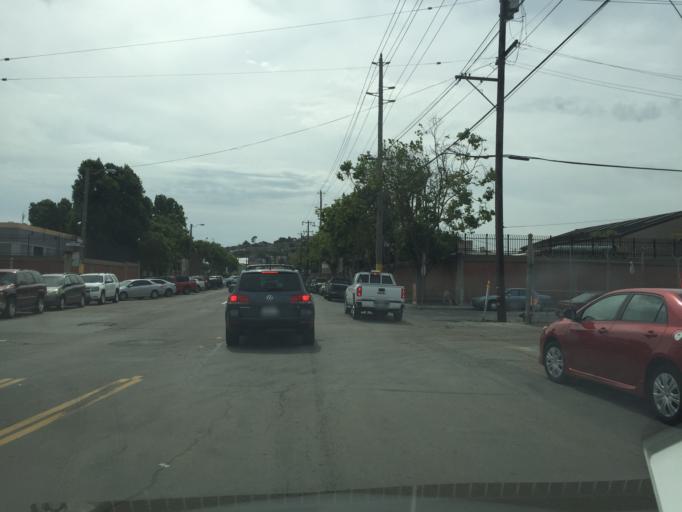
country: US
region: California
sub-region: San Francisco County
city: San Francisco
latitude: 37.7411
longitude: -122.3935
